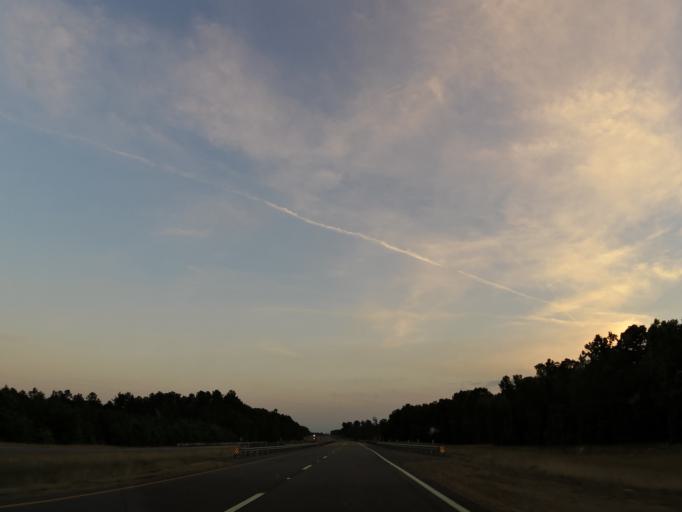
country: US
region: Mississippi
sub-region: Kemper County
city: De Kalb
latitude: 32.7601
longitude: -88.4656
